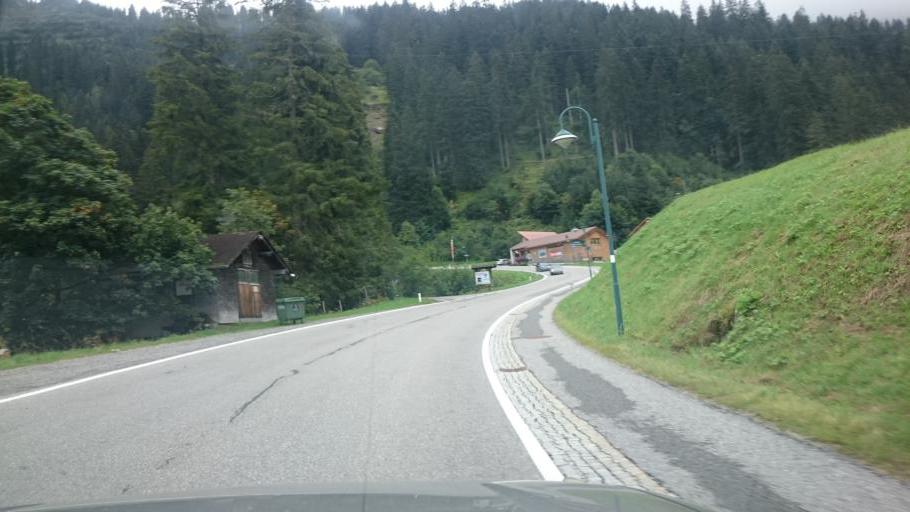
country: AT
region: Vorarlberg
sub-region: Politischer Bezirk Bregenz
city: Schroecken
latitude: 47.2580
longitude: 10.0928
